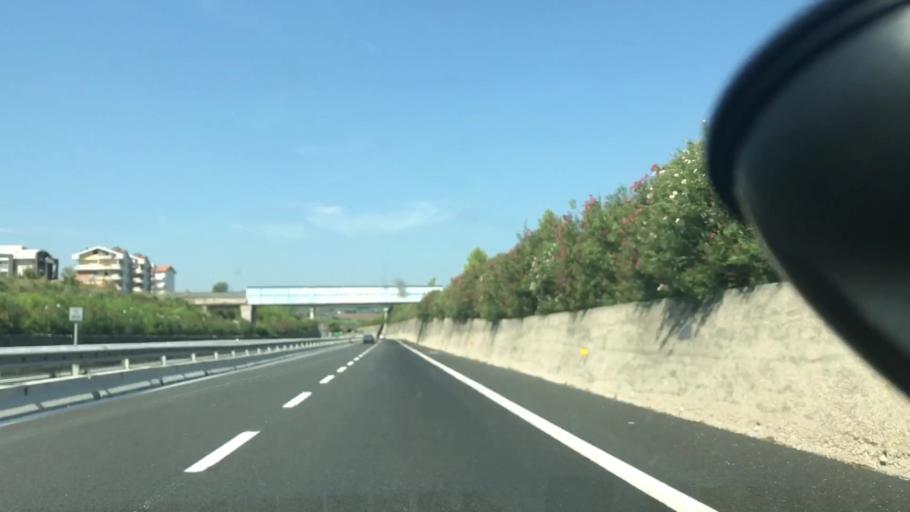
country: IT
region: Abruzzo
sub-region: Provincia di Chieti
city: San Salvo
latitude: 42.0586
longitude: 14.7438
